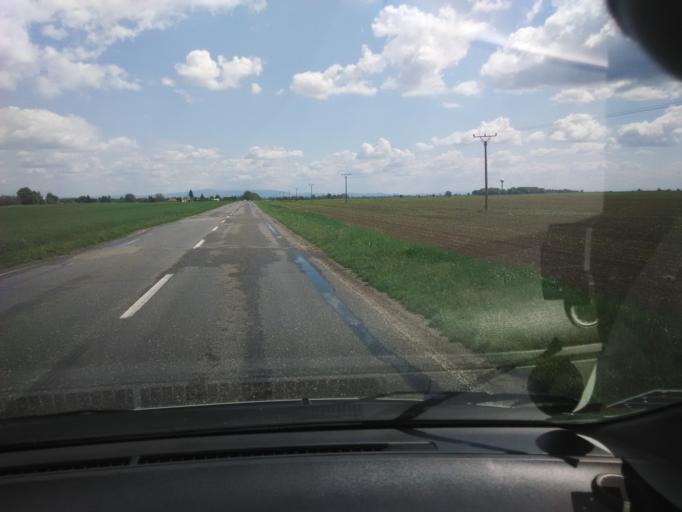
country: SK
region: Nitriansky
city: Levice
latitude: 48.1712
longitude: 18.5395
